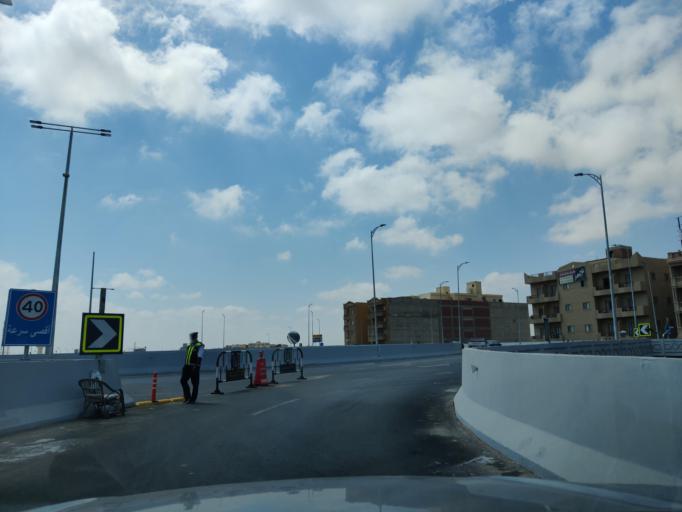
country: EG
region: Muhafazat Matruh
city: Al `Alamayn
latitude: 30.8393
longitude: 28.9528
